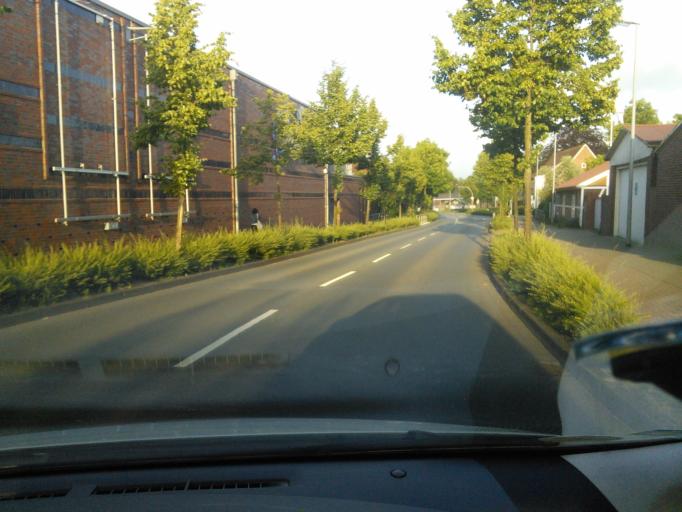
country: DE
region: Lower Saxony
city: Stade
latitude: 53.6019
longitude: 9.4799
